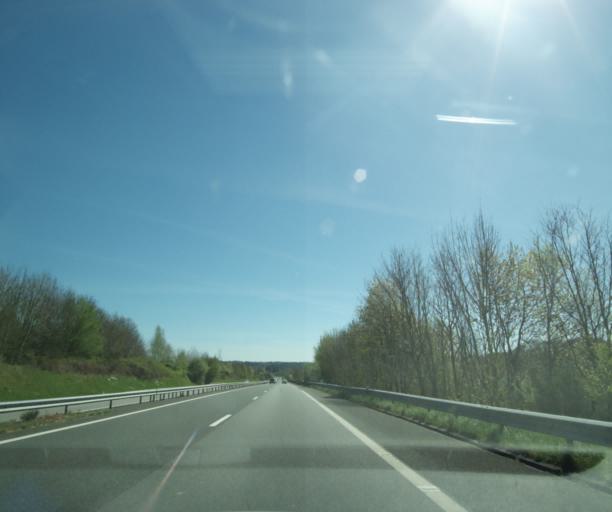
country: FR
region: Limousin
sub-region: Departement de la Correze
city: Vigeois
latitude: 45.4268
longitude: 1.5140
